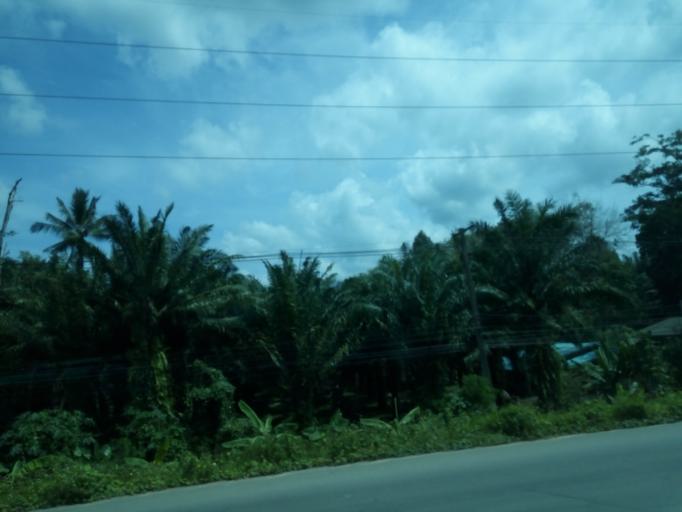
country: TH
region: Phangnga
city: Ban Ao Nang
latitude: 8.2053
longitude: 98.8165
